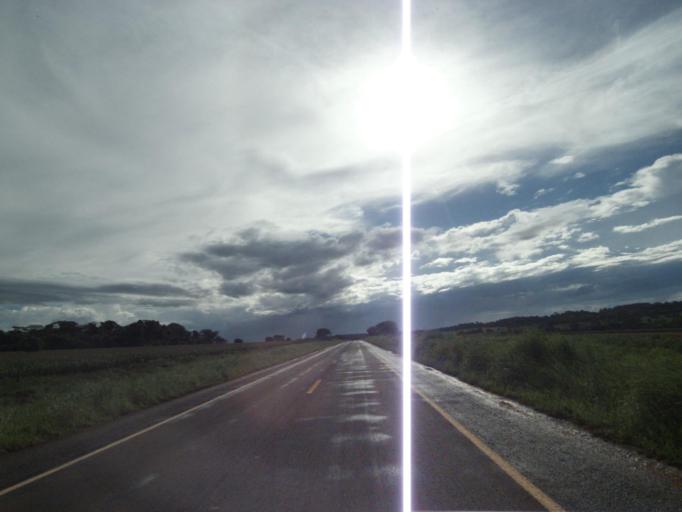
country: BR
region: Goias
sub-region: Jaragua
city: Jaragua
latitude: -15.9043
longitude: -49.5455
